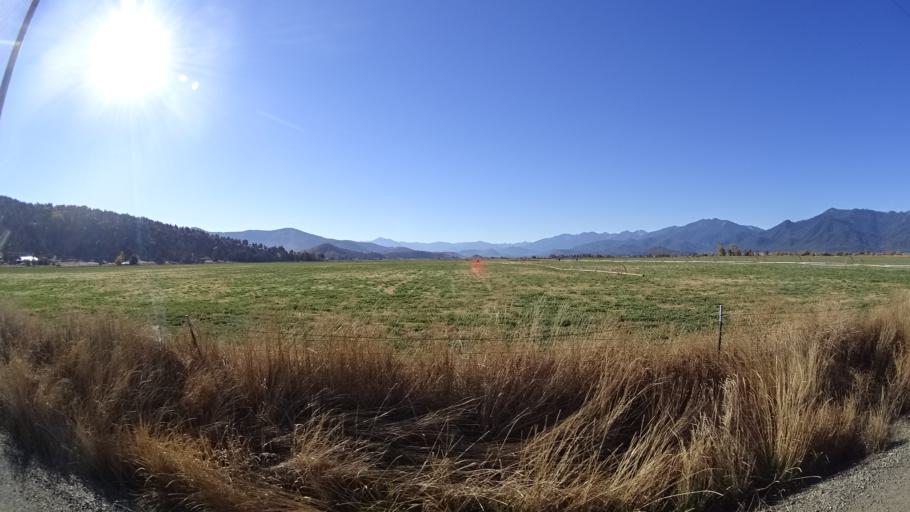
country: US
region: California
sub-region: Siskiyou County
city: Yreka
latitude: 41.5198
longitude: -122.8448
